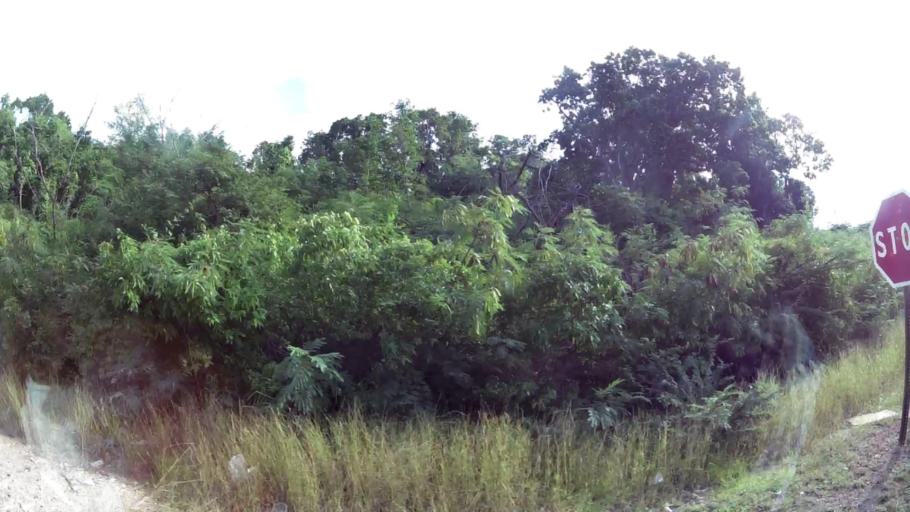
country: AG
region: Saint George
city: Piggotts
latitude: 17.1444
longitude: -61.8105
